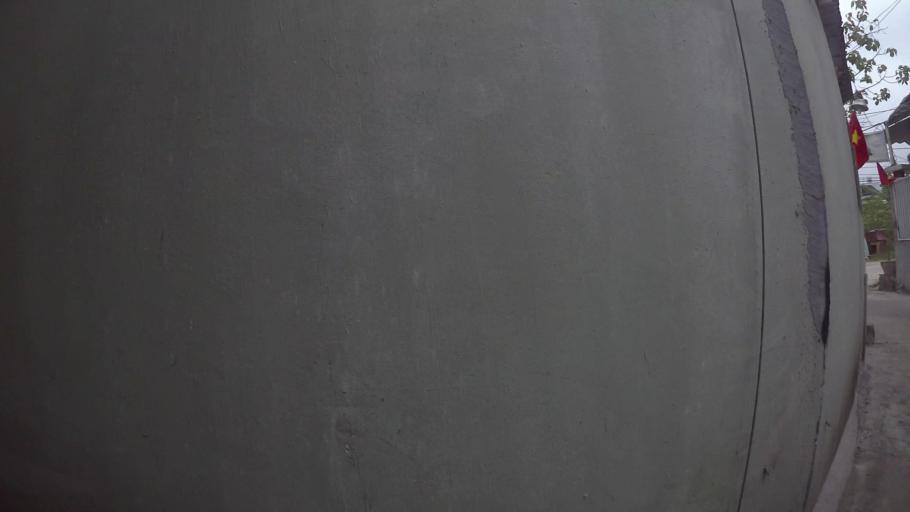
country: VN
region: Da Nang
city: Lien Chieu
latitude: 16.0657
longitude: 108.1689
